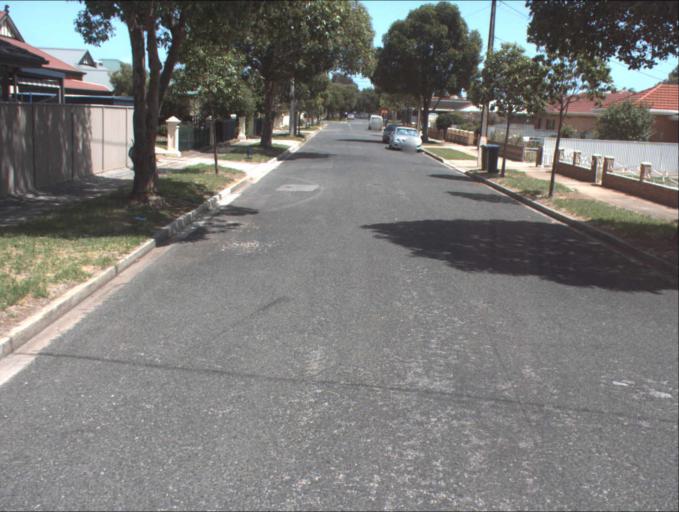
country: AU
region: South Australia
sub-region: Charles Sturt
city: Woodville North
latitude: -34.8627
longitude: 138.5625
